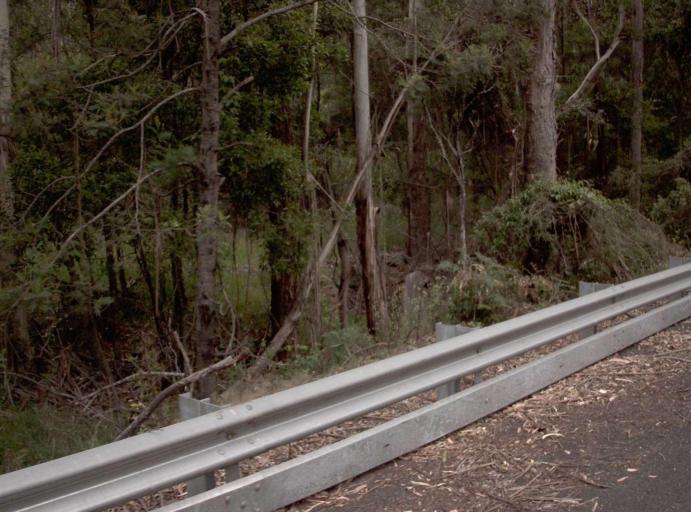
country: AU
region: New South Wales
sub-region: Bombala
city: Bombala
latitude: -37.4080
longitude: 149.1984
